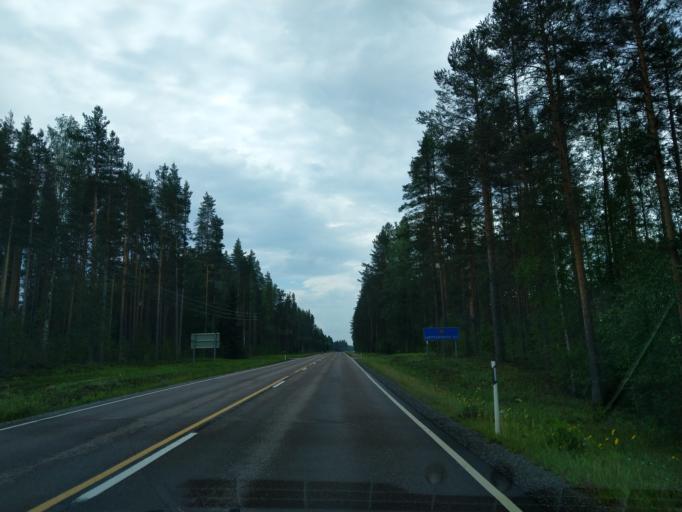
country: FI
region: Southern Savonia
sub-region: Savonlinna
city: Punkaharju
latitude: 61.6535
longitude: 29.4205
